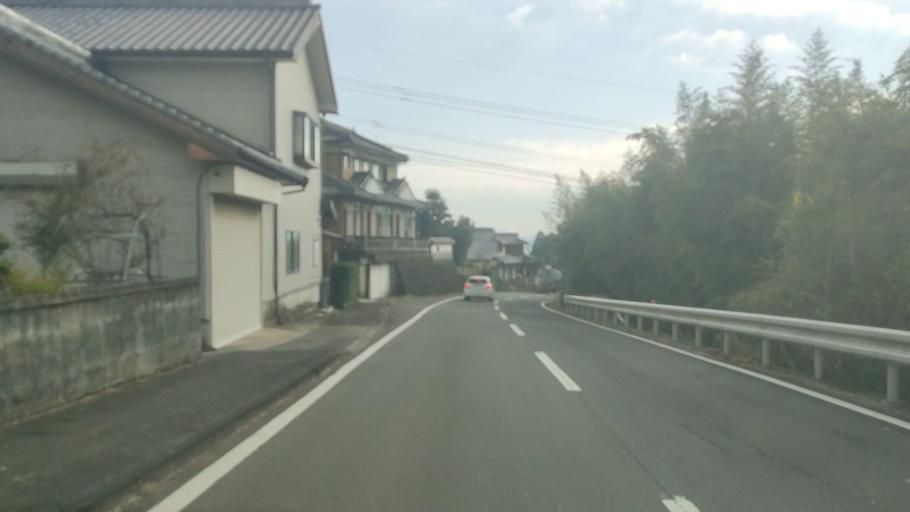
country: JP
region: Nagasaki
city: Shimabara
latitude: 32.6746
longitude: 130.2816
